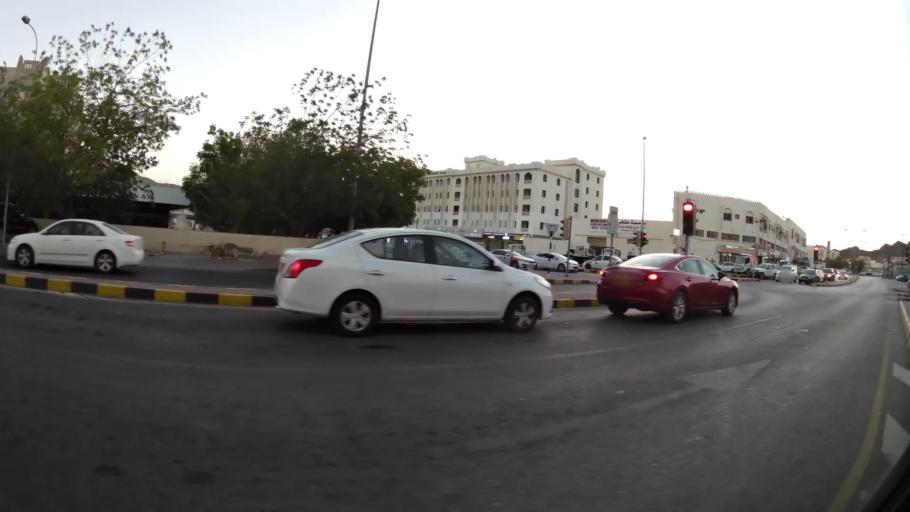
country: OM
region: Muhafazat Masqat
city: Muscat
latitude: 23.5885
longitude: 58.5624
